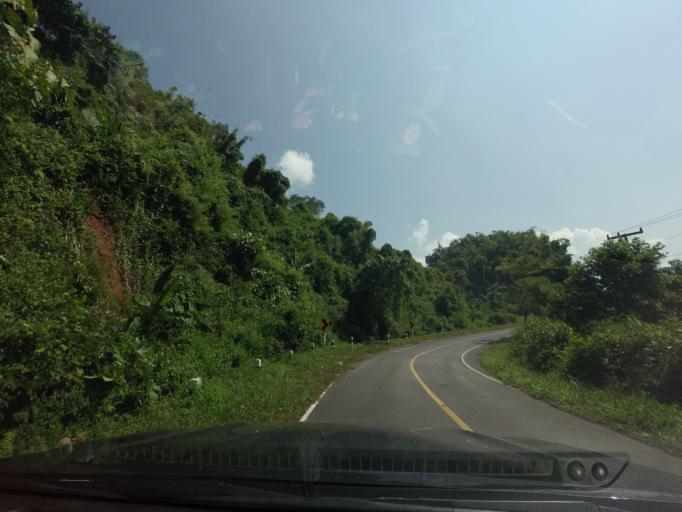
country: TH
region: Nan
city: Bo Kluea
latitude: 19.0239
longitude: 101.1817
